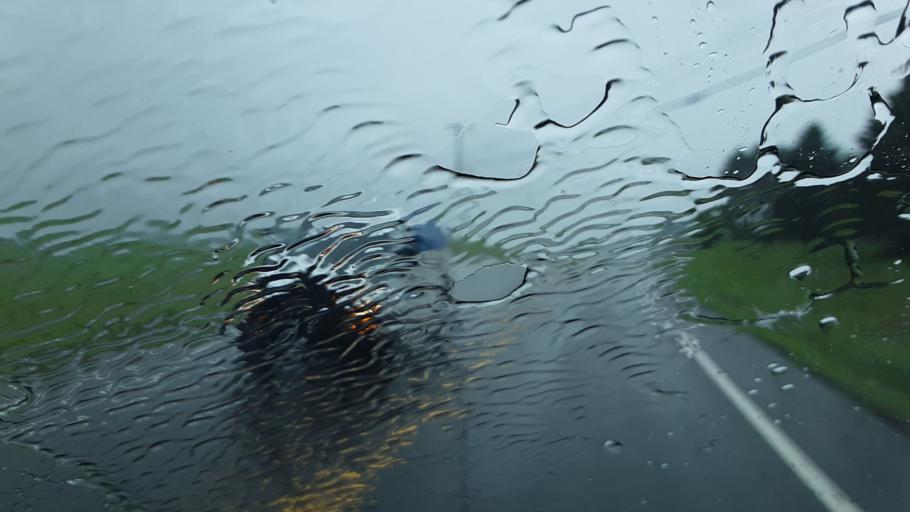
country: US
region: Maine
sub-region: Aroostook County
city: Presque Isle
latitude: 46.5910
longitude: -68.3857
